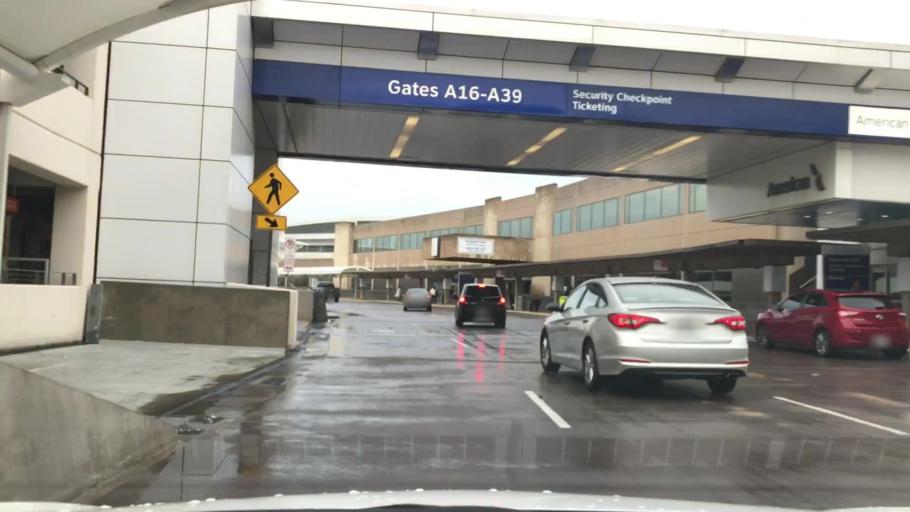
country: US
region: Texas
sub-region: Tarrant County
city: Grapevine
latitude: 32.9046
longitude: -97.0362
